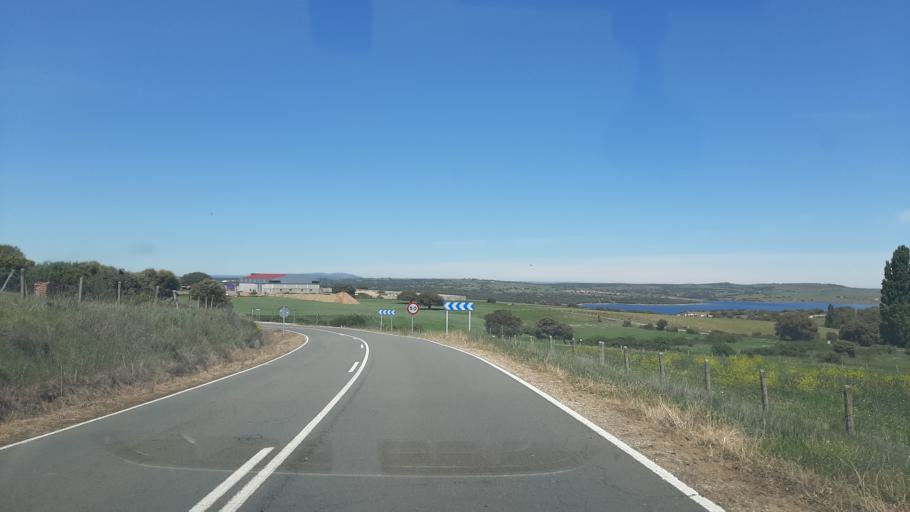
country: ES
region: Castille and Leon
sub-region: Provincia de Salamanca
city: Aldeavieja de Tormes
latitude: 40.5465
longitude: -5.5956
